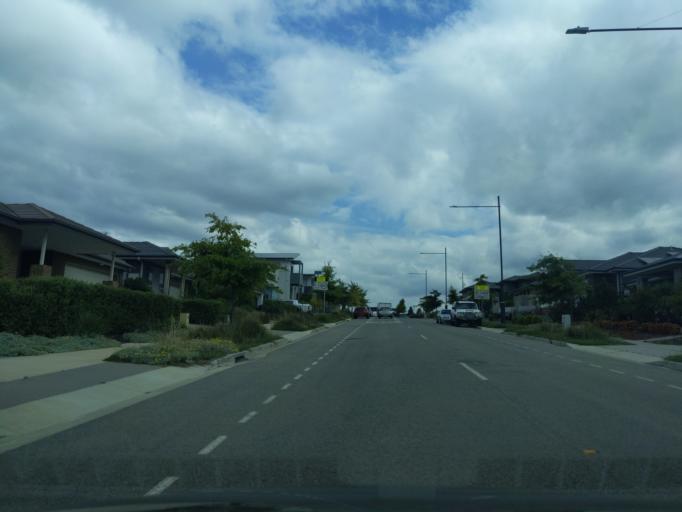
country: AU
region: New South Wales
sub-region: Queanbeyan
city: Queanbeyan
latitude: -35.4206
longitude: 149.2340
